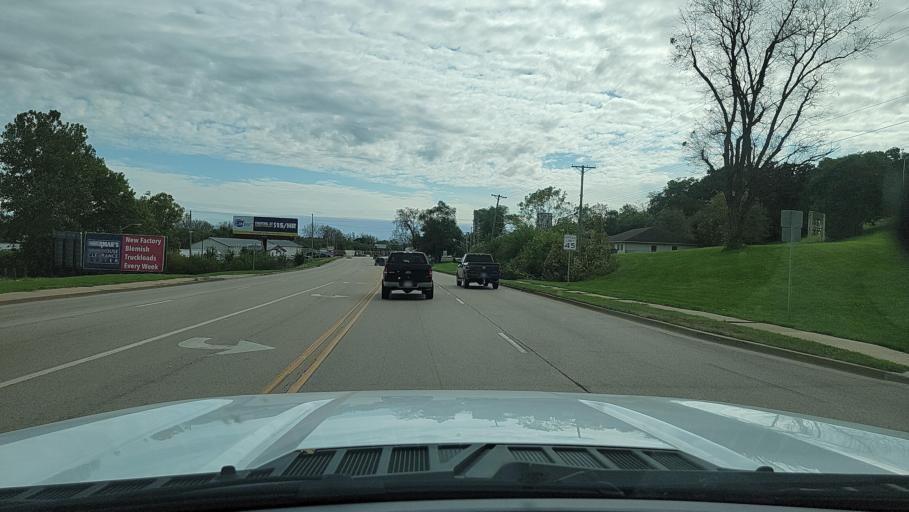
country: US
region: Illinois
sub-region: Peoria County
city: Bartonville
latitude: 40.6390
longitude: -89.6521
